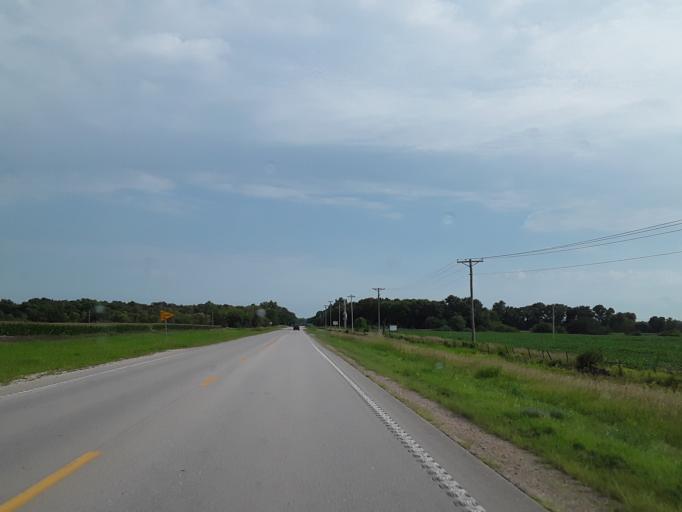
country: US
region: Nebraska
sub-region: Saunders County
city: Ashland
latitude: 41.0634
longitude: -96.3681
